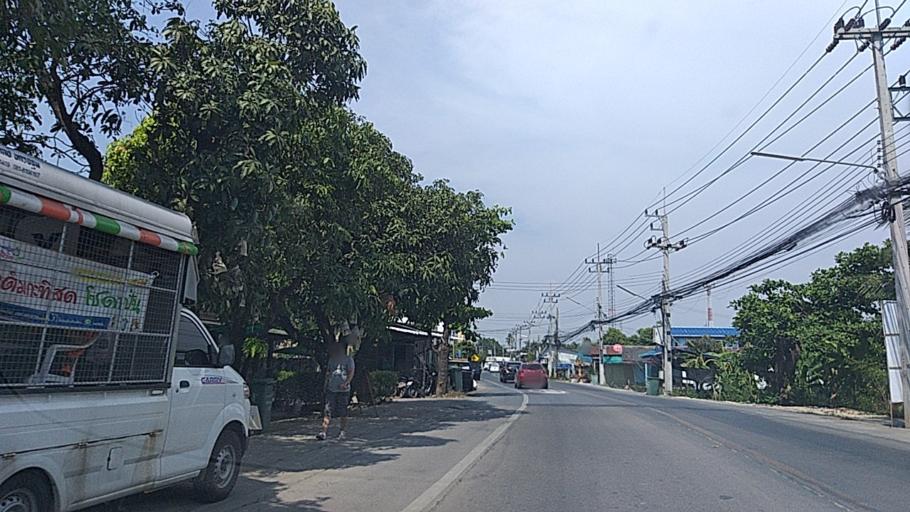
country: TH
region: Nakhon Pathom
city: Sam Phran
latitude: 13.7454
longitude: 100.2748
